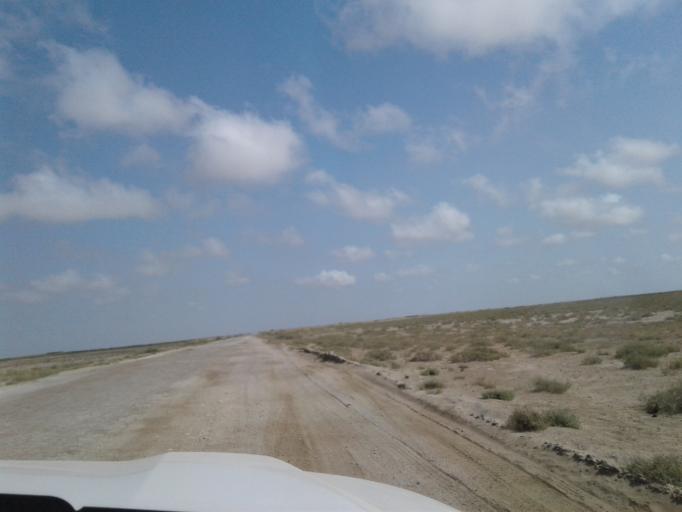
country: IR
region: Golestan
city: Gomishan
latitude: 37.6203
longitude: 53.9273
